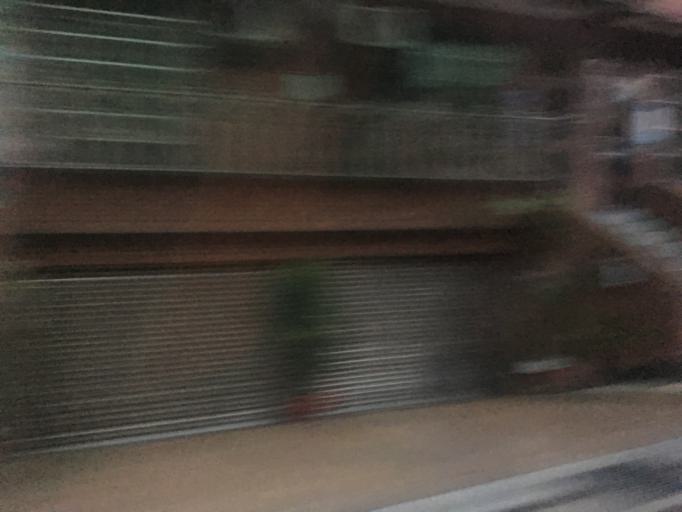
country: TW
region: Taiwan
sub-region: Hsinchu
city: Hsinchu
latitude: 24.7949
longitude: 120.9577
